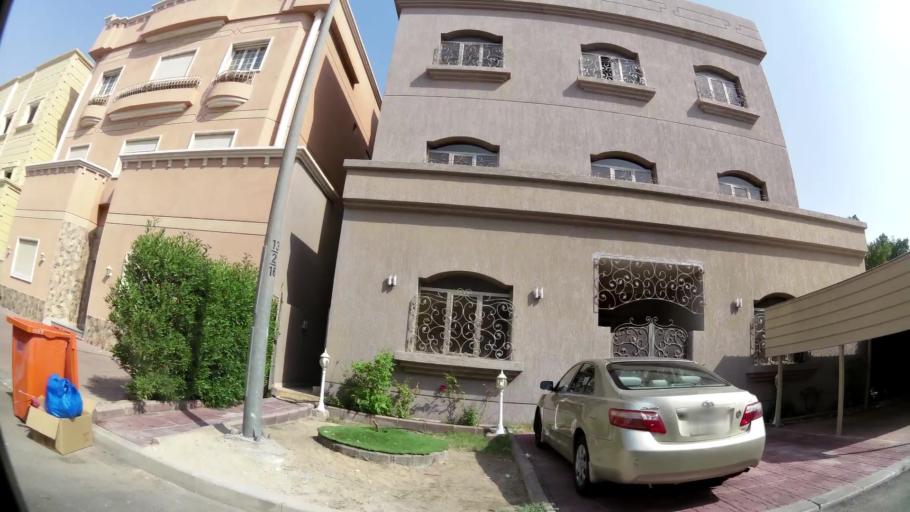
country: KW
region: Muhafazat al Jahra'
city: Al Jahra'
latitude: 29.3262
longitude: 47.7761
